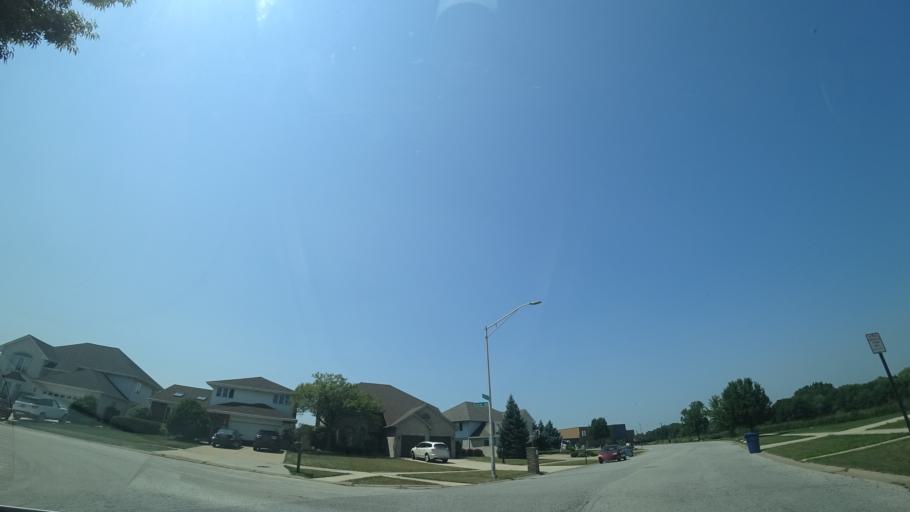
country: US
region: Illinois
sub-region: Cook County
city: Oak Lawn
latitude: 41.6971
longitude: -87.7536
